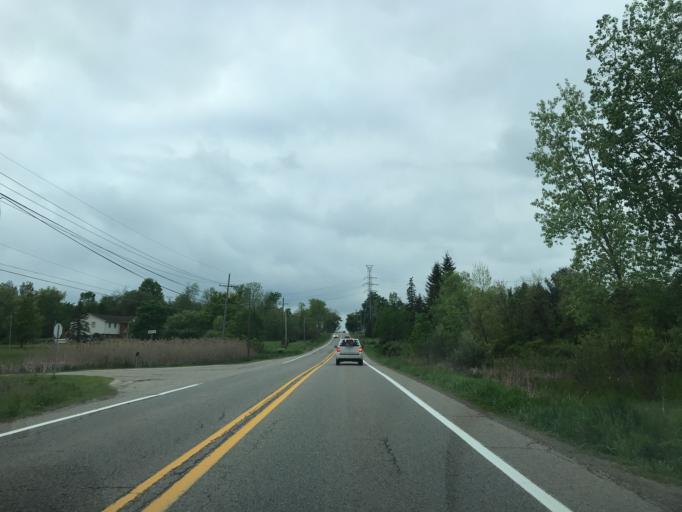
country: US
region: Michigan
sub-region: Oakland County
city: South Lyon
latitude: 42.4617
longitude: -83.6197
